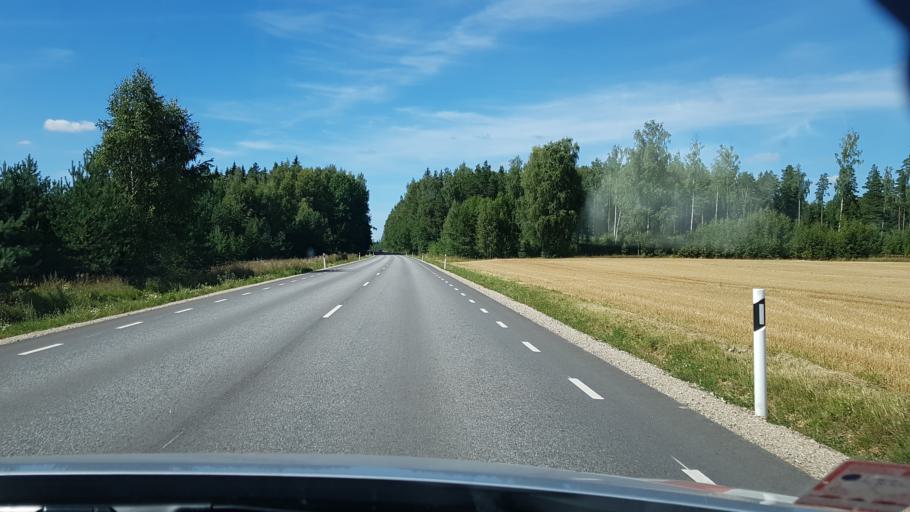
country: EE
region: Polvamaa
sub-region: Polva linn
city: Polva
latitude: 58.0295
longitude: 27.1521
